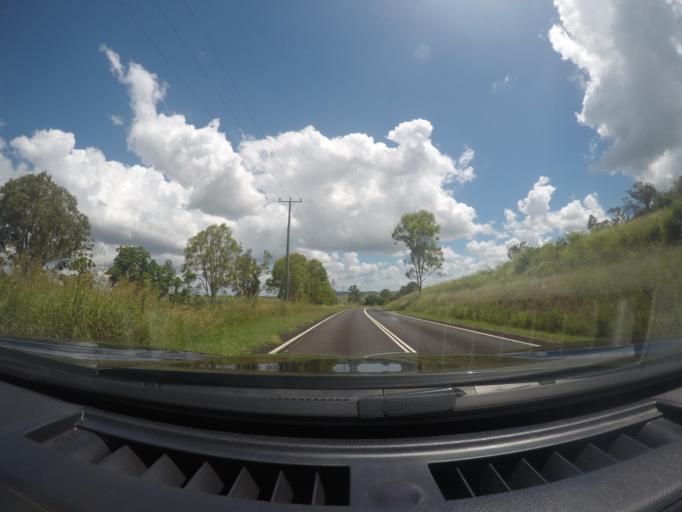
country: AU
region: Queensland
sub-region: Moreton Bay
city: D'Aguilar
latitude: -27.1454
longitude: 152.5528
